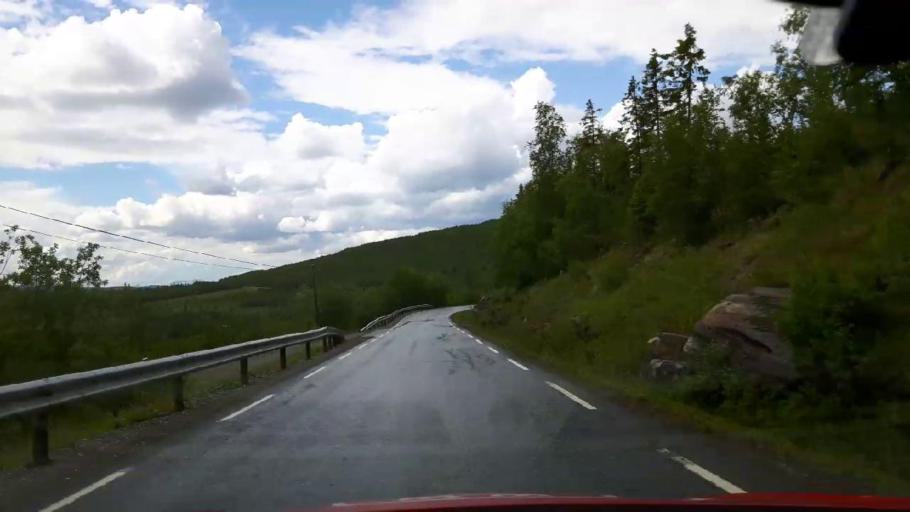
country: NO
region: Nord-Trondelag
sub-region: Lierne
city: Sandvika
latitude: 64.1116
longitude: 13.9731
